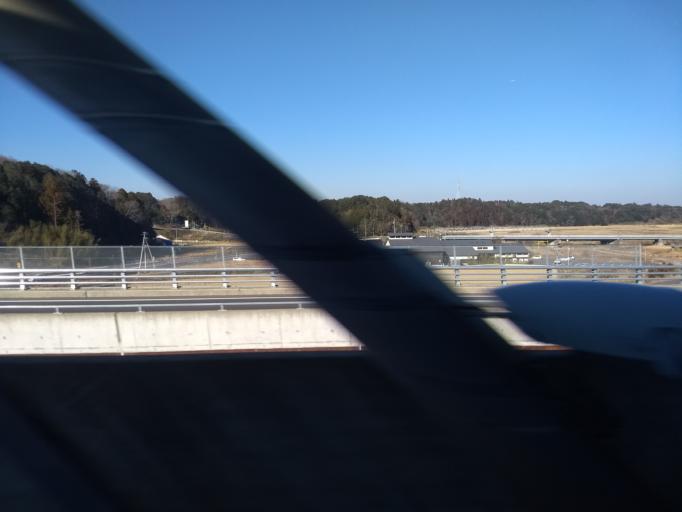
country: JP
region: Chiba
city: Narita
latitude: 35.7998
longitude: 140.2984
